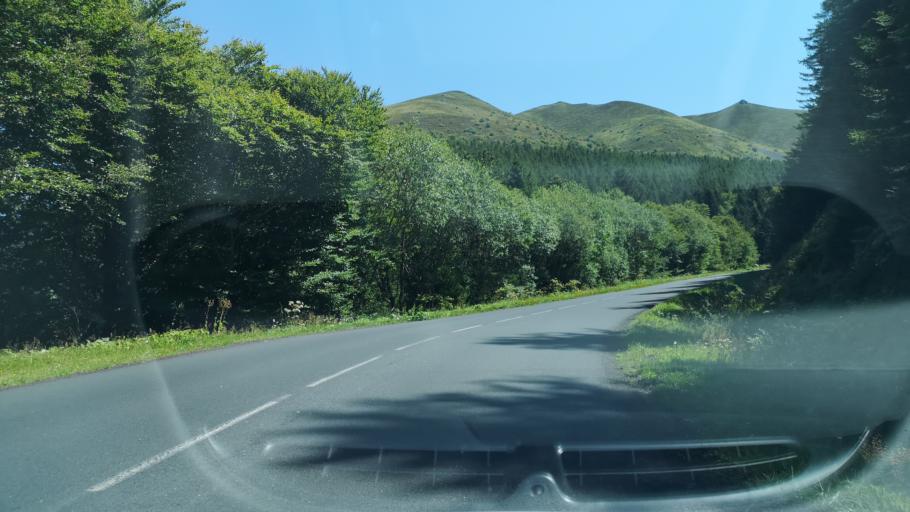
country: FR
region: Auvergne
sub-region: Departement du Puy-de-Dome
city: Mont-Dore
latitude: 45.5927
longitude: 2.8291
